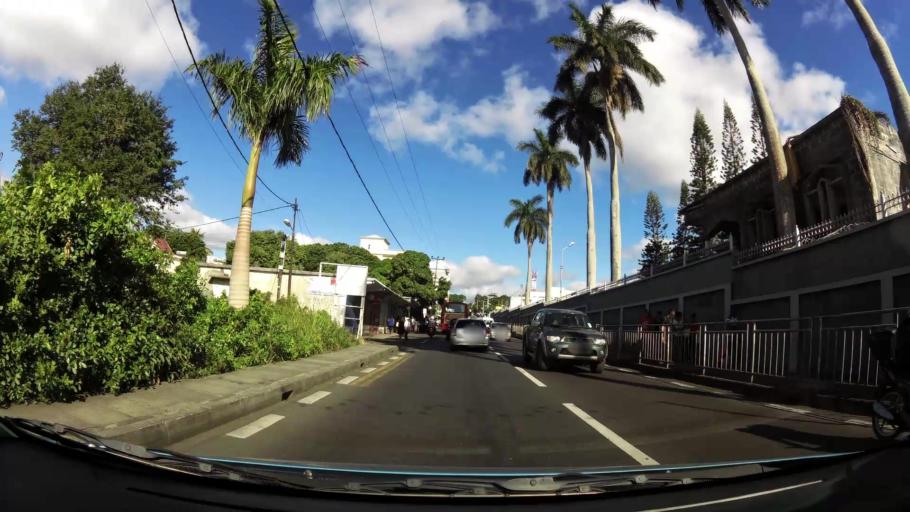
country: MU
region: Plaines Wilhems
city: Quatre Bornes
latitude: -20.2772
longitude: 57.4772
